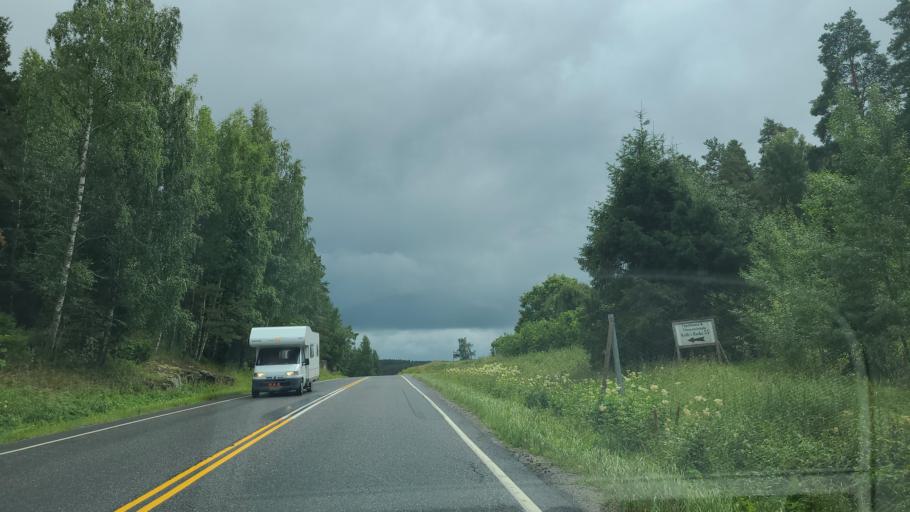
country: FI
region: Varsinais-Suomi
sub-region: Turku
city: Sauvo
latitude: 60.3376
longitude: 22.7022
